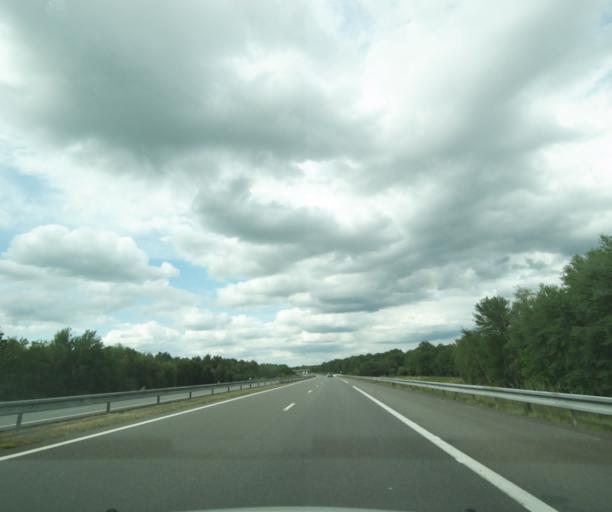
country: FR
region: Centre
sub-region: Departement du Loir-et-Cher
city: Theillay
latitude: 47.3643
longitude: 2.0533
